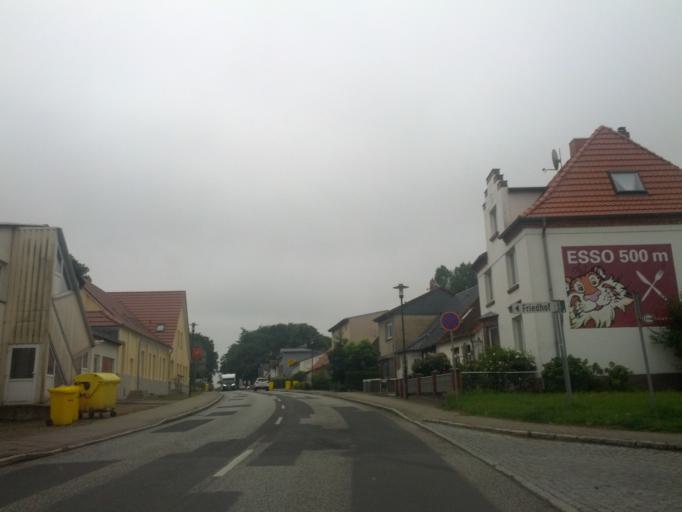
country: DE
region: Mecklenburg-Vorpommern
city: Neubukow
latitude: 54.0285
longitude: 11.6666
